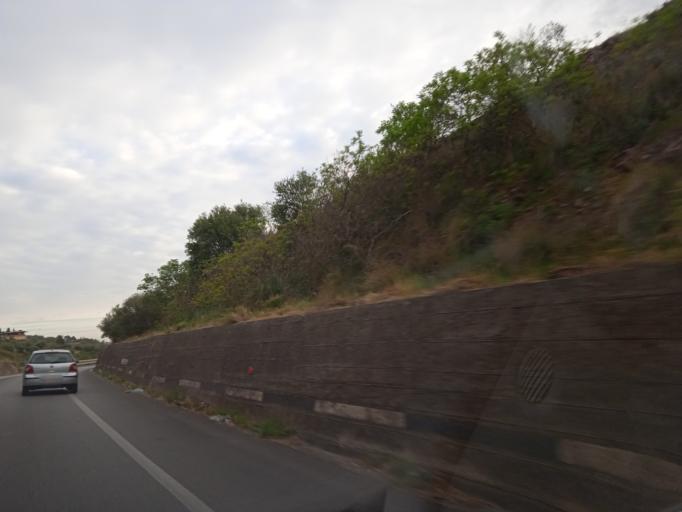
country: IT
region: Sicily
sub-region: Palermo
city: Misilmeri
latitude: 38.0465
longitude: 13.4602
